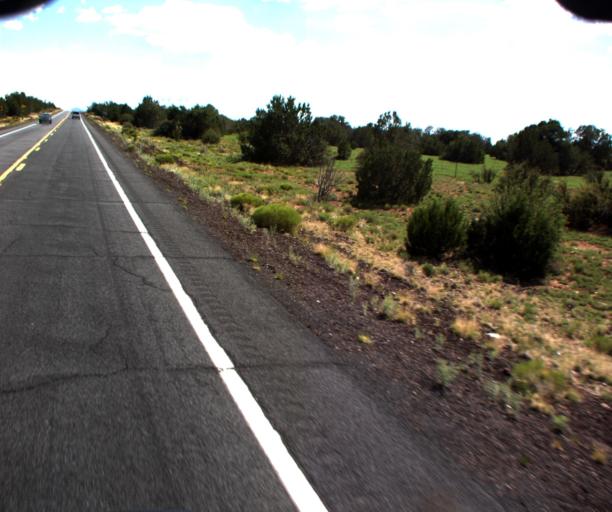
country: US
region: Arizona
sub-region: Coconino County
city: Williams
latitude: 35.4545
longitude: -112.1705
